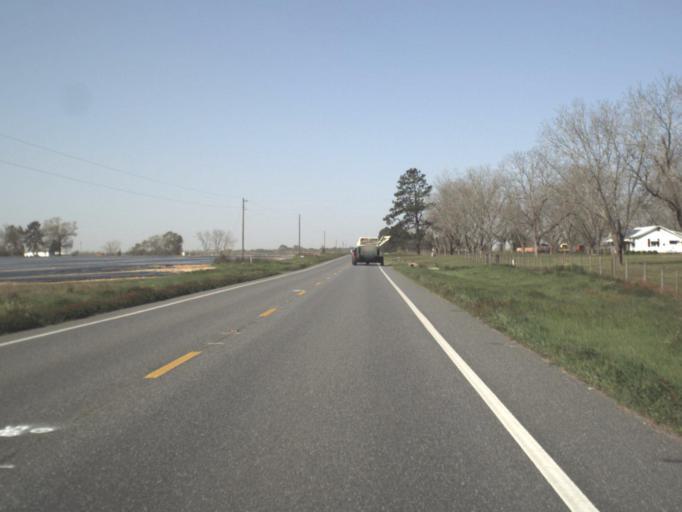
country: US
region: Florida
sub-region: Jackson County
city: Malone
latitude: 30.9539
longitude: -85.2327
